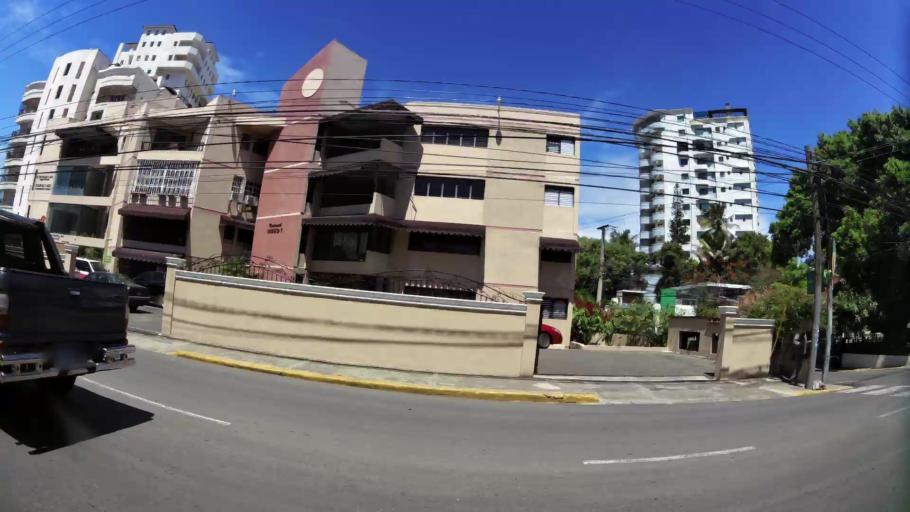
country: DO
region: Santiago
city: Santiago de los Caballeros
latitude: 19.4537
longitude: -70.6888
